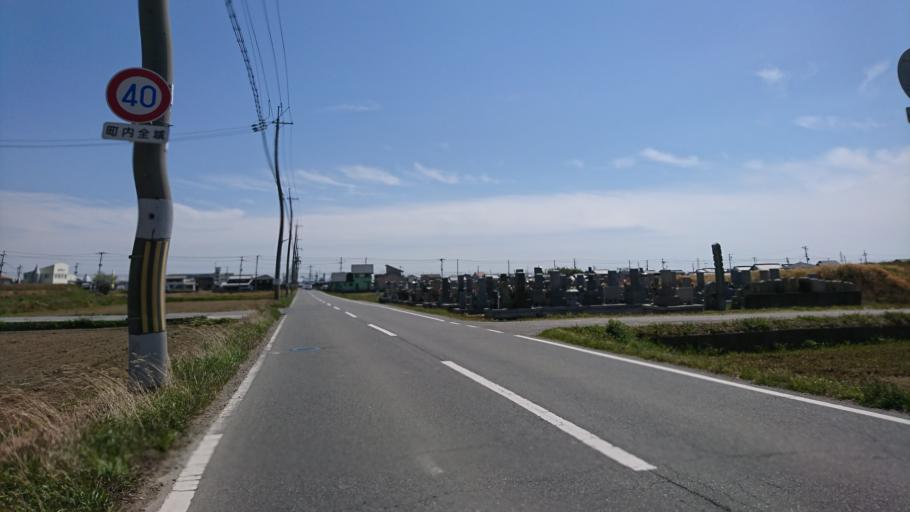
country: JP
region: Hyogo
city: Kakogawacho-honmachi
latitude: 34.7462
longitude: 134.8897
